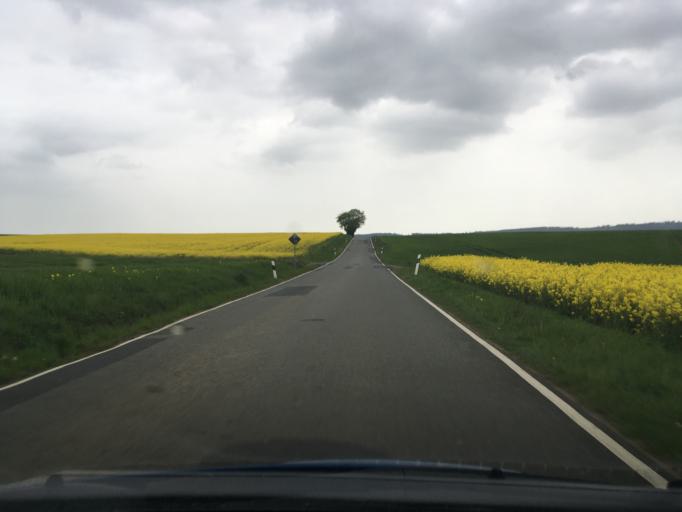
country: DE
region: Lower Saxony
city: Eimen
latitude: 51.8538
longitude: 9.8112
